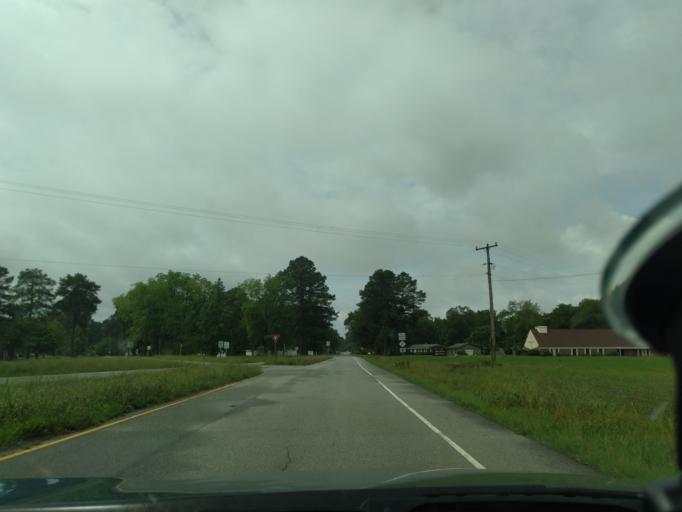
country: US
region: North Carolina
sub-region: Washington County
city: Plymouth
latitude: 35.8844
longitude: -76.6098
